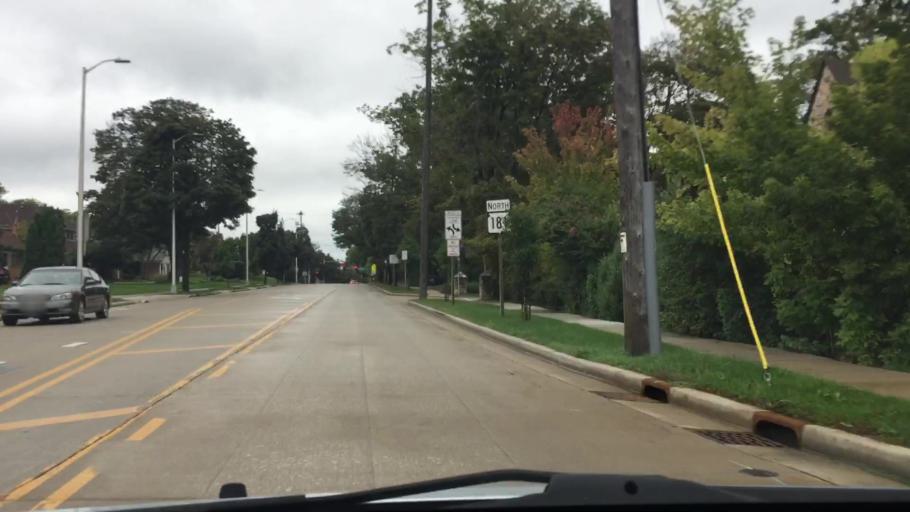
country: US
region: Wisconsin
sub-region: Milwaukee County
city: Wauwatosa
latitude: 43.0365
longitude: -88.0159
